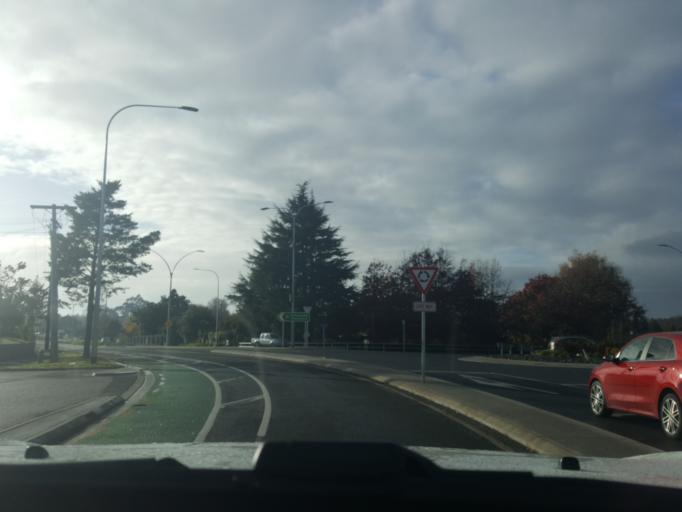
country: NZ
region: Waikato
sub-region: Hamilton City
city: Hamilton
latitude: -37.8009
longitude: 175.3220
